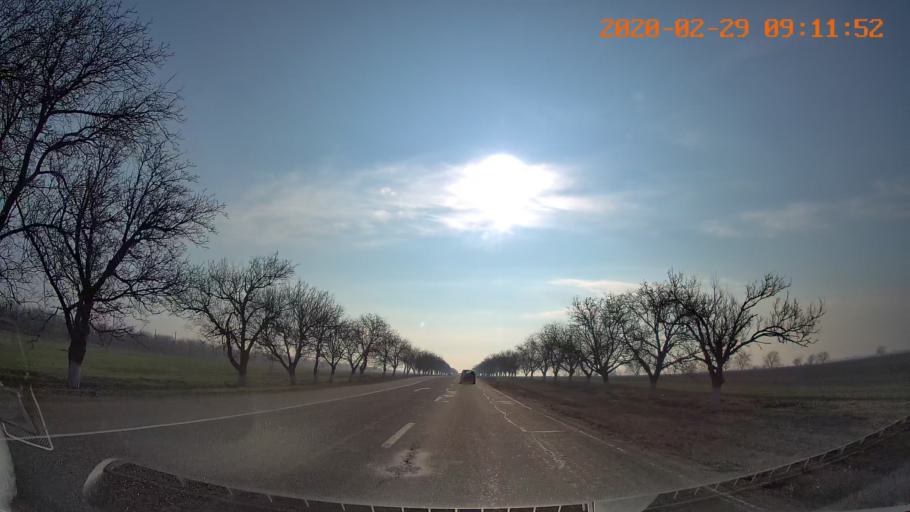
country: MD
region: Telenesti
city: Slobozia
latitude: 46.8314
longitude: 29.8072
